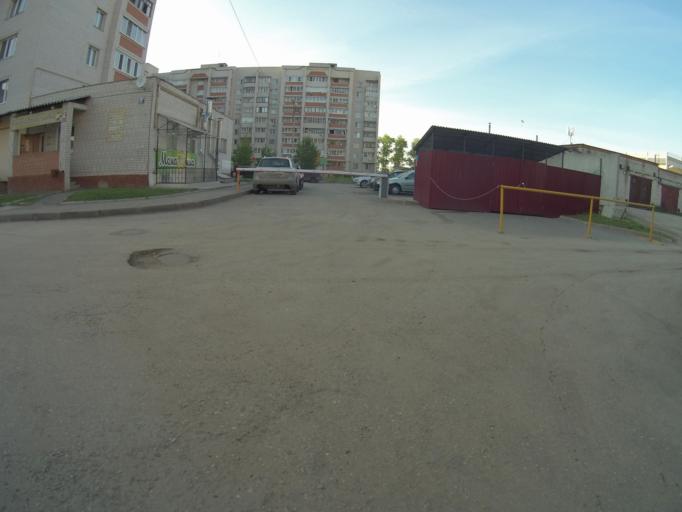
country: RU
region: Vladimir
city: Kommunar
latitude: 56.1714
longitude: 40.4466
